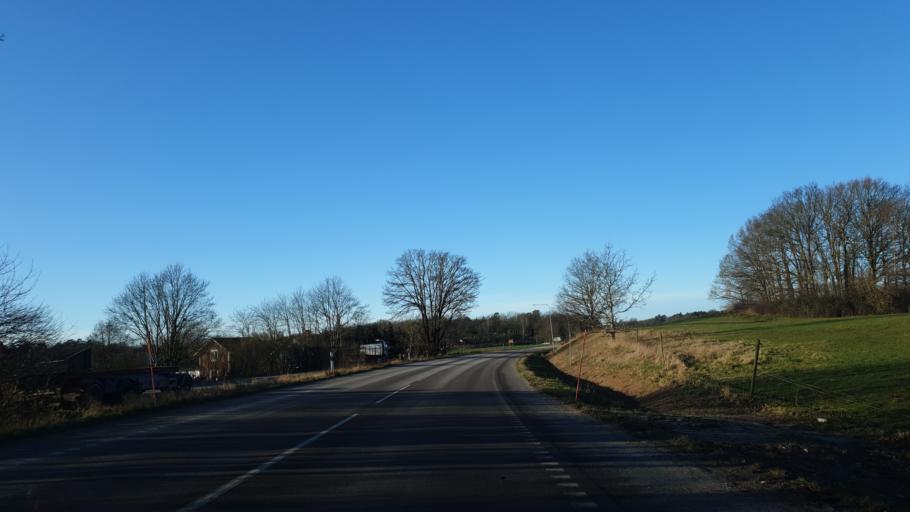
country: SE
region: Blekinge
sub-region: Ronneby Kommun
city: Ronneby
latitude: 56.1919
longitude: 15.3552
